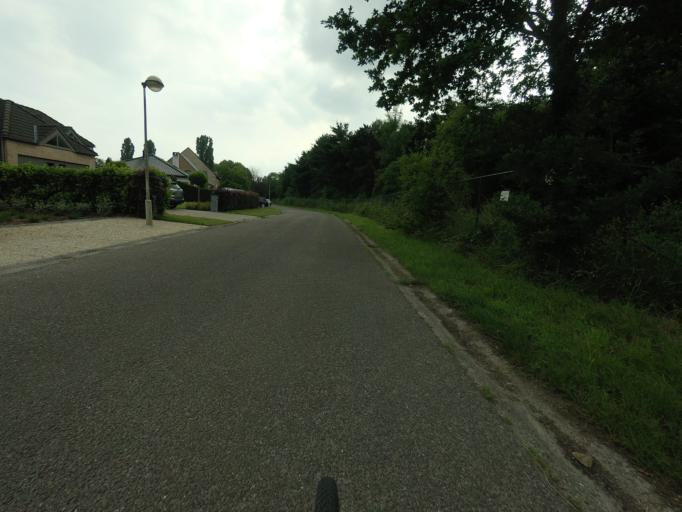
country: BE
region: Flanders
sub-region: Provincie Antwerpen
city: Schilde
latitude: 51.2185
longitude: 4.5806
